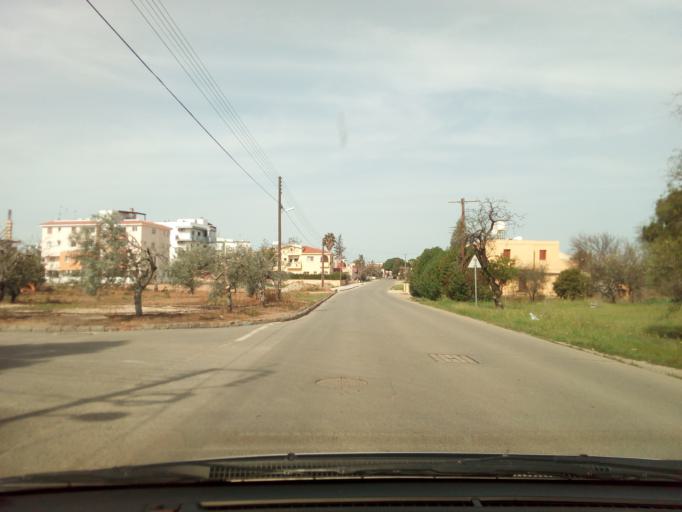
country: CY
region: Lefkosia
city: Tseri
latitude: 35.1017
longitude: 33.3064
